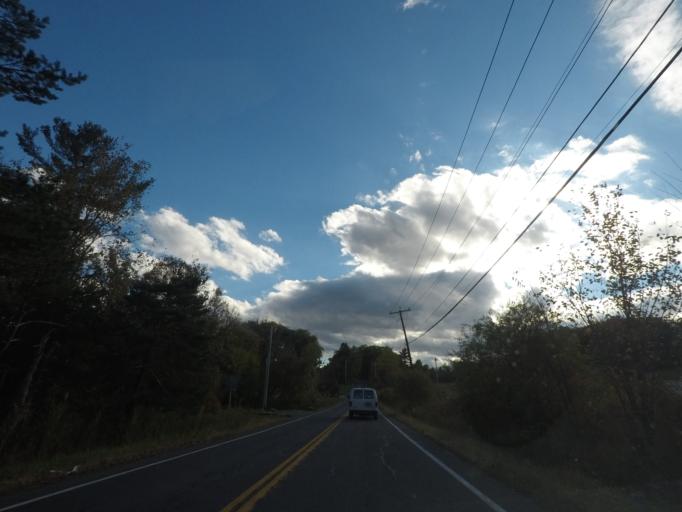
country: US
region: New York
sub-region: Schenectady County
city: Niskayuna
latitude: 42.7658
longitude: -73.8289
